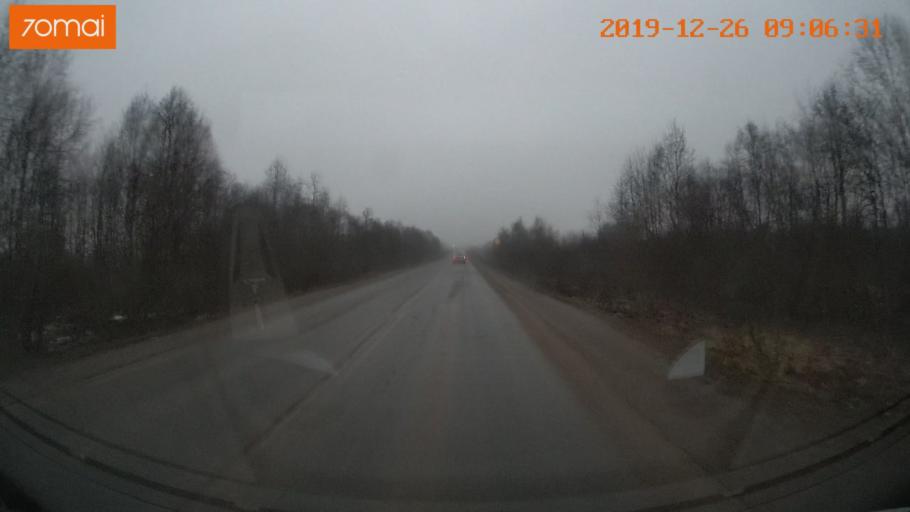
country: RU
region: Vologda
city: Gryazovets
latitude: 58.8370
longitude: 40.2528
